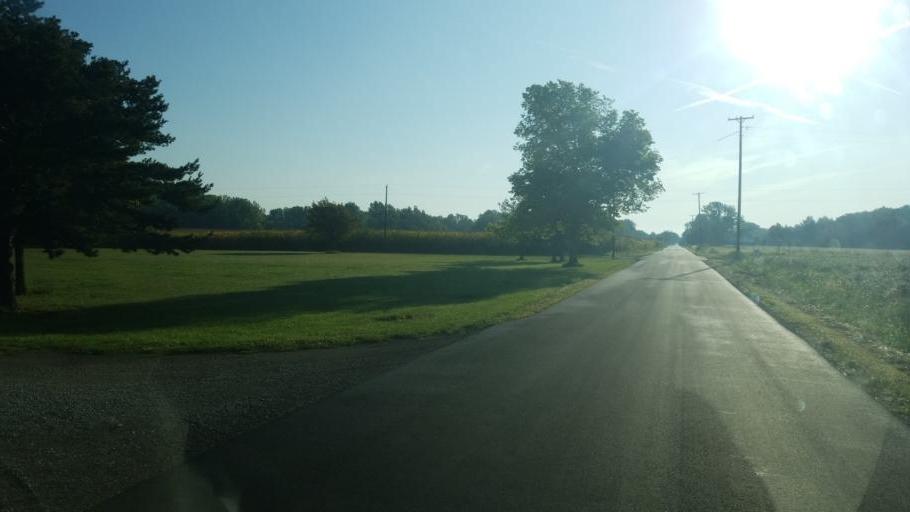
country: US
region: Ohio
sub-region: Morrow County
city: Mount Gilead
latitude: 40.6160
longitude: -82.9006
